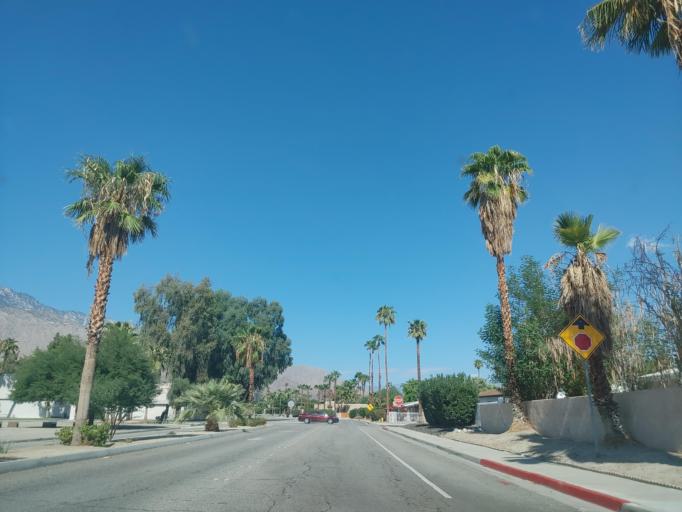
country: US
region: California
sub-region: Riverside County
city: Palm Springs
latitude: 33.8101
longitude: -116.5067
